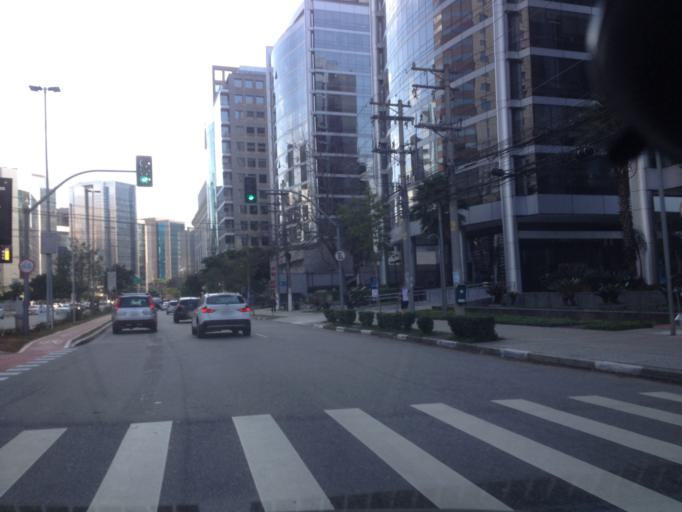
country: BR
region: Sao Paulo
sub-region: Sao Paulo
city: Sao Paulo
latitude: -23.5952
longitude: -46.6839
